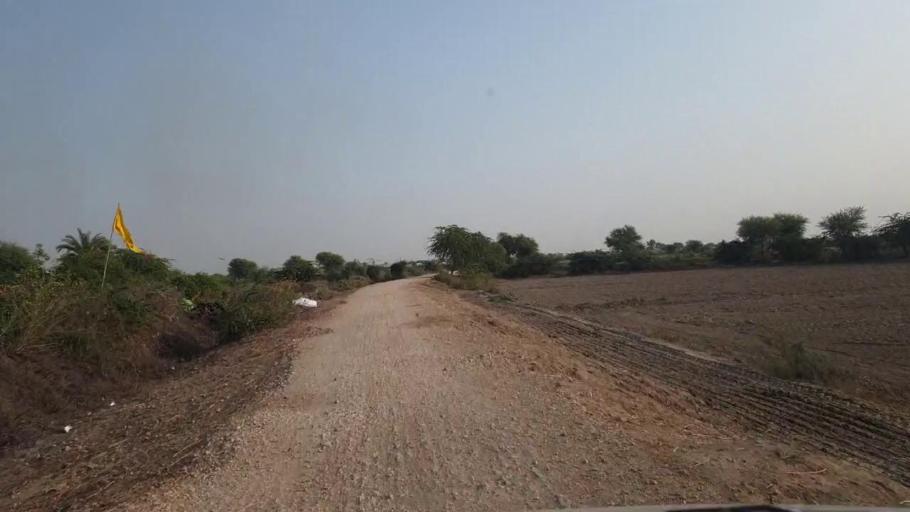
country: PK
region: Sindh
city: Rajo Khanani
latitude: 25.0228
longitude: 68.7812
